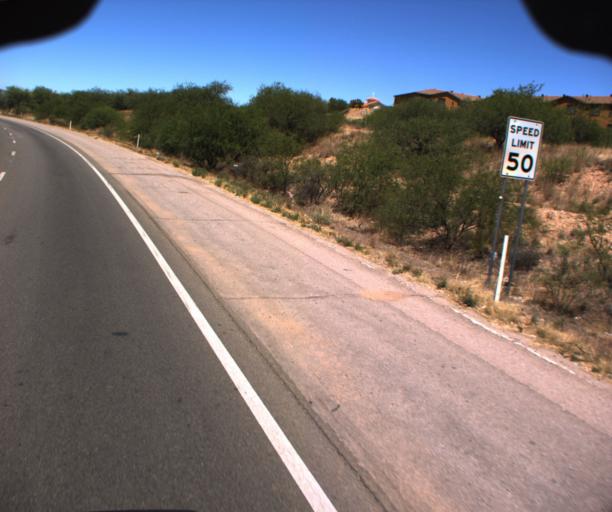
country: US
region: Arizona
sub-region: Santa Cruz County
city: Nogales
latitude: 31.3631
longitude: -110.9522
